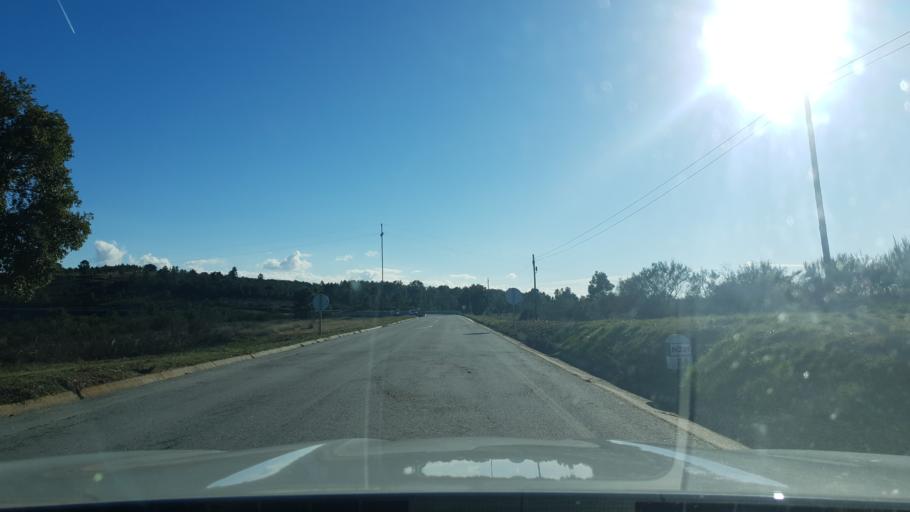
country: PT
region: Braganca
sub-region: Freixo de Espada A Cinta
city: Freixo de Espada a Cinta
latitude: 41.1218
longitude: -6.8201
